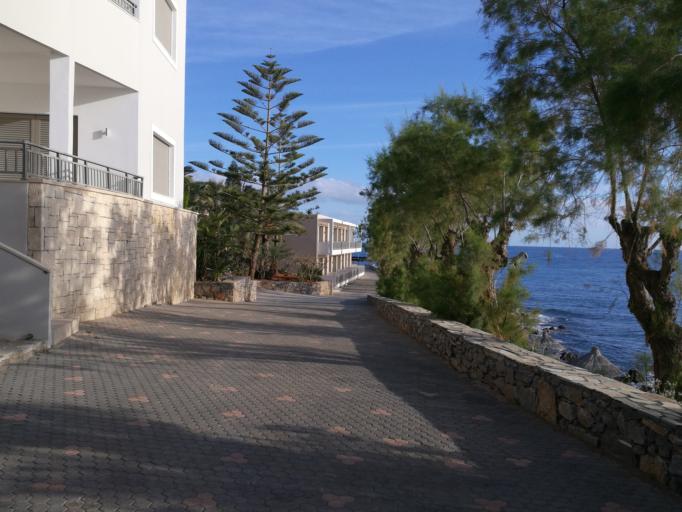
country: GR
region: Crete
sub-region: Nomos Irakleiou
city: Stalis
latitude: 35.3035
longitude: 25.4224
